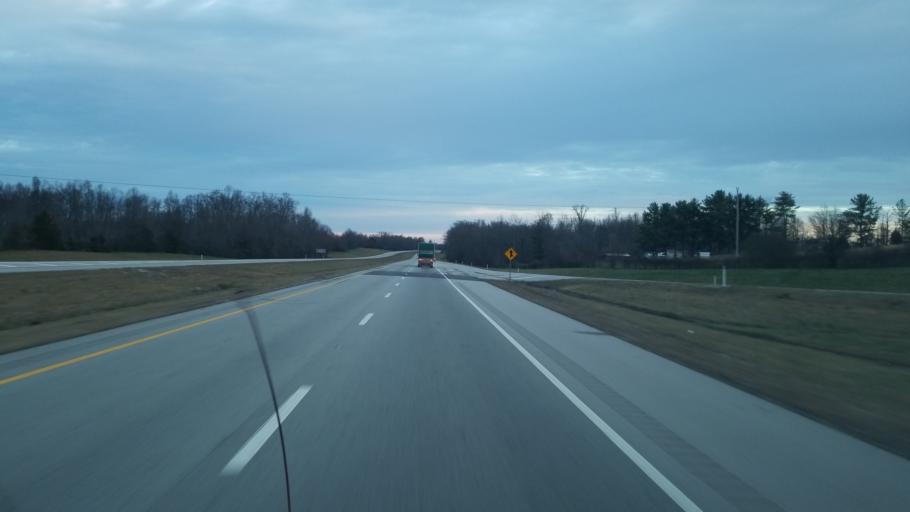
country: US
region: Tennessee
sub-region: White County
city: Sparta
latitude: 36.0198
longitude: -85.5082
